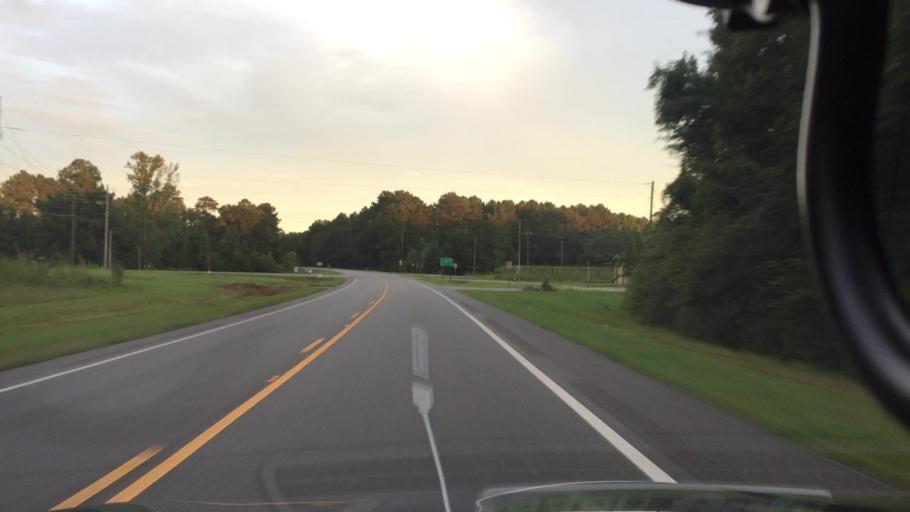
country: US
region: Alabama
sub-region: Coffee County
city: New Brockton
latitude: 31.4908
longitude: -85.9141
